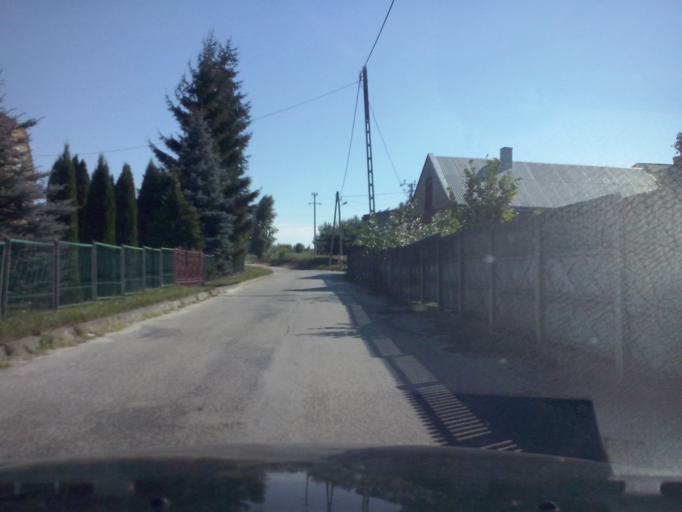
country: PL
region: Swietokrzyskie
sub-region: Powiat kielecki
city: Chmielnik
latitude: 50.6111
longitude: 20.7339
